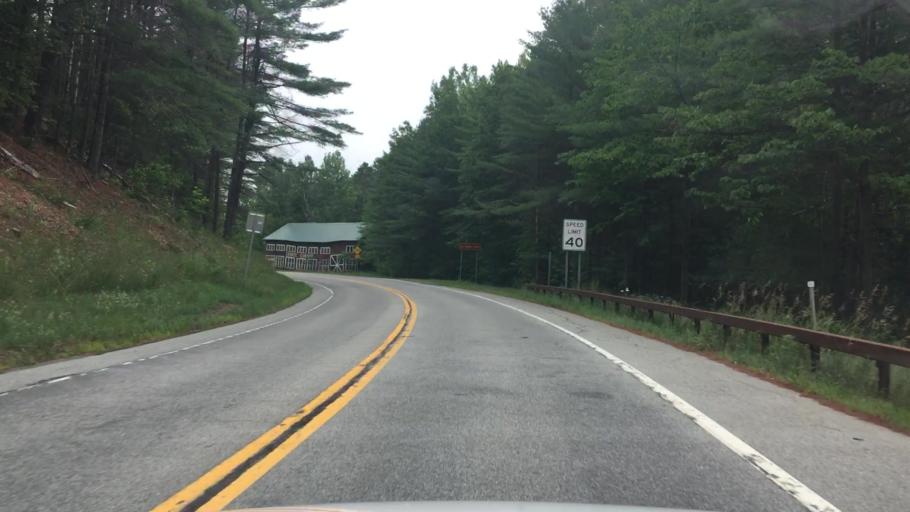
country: US
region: New York
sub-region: Essex County
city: Keeseville
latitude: 44.4282
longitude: -73.6797
